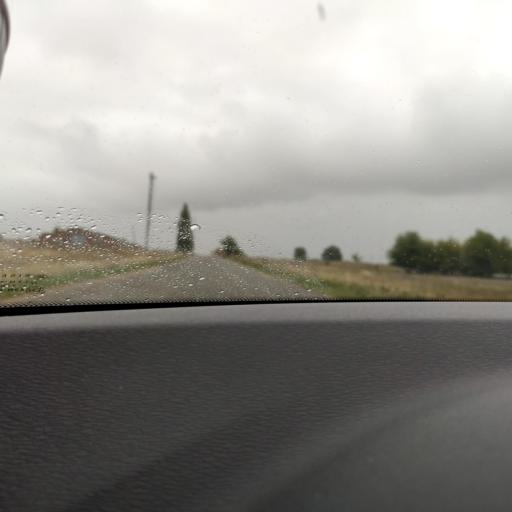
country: RU
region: Samara
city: Yelkhovka
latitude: 53.7444
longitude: 50.2381
